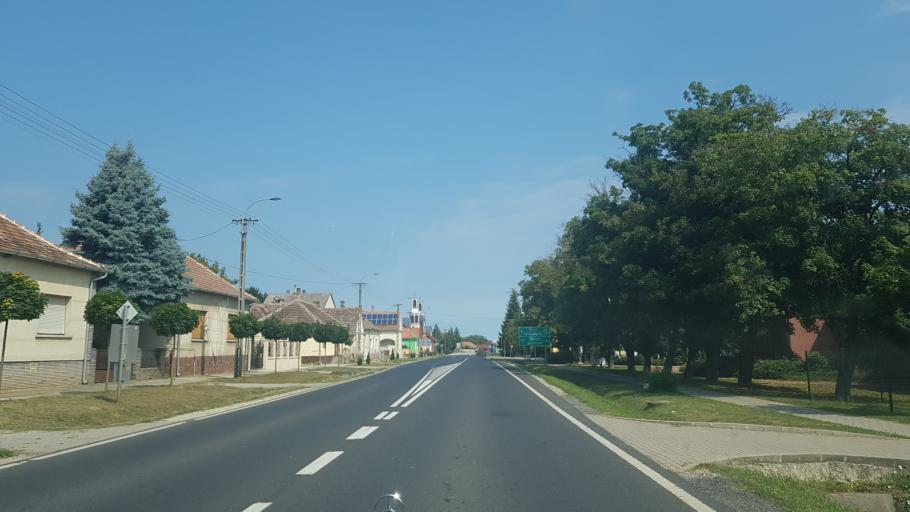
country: HU
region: Somogy
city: Bohonye
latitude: 46.4053
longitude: 17.3860
